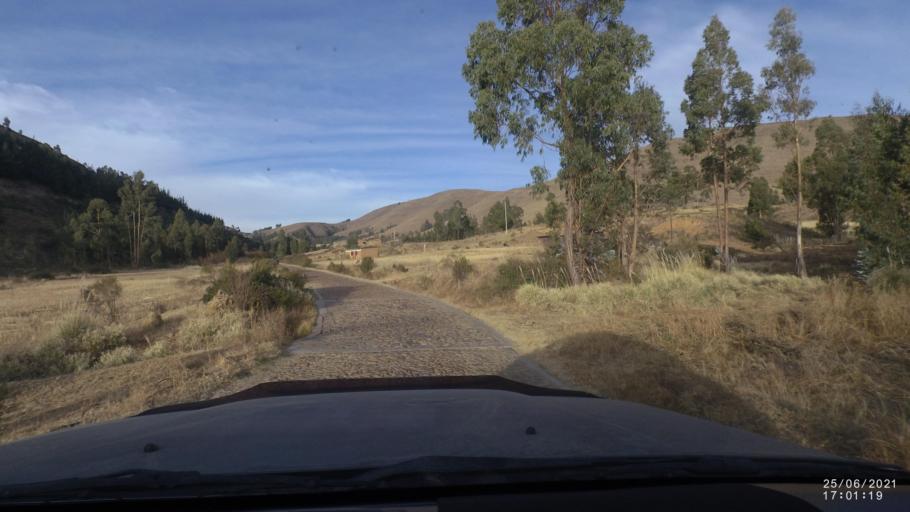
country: BO
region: Cochabamba
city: Arani
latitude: -17.8376
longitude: -65.7418
